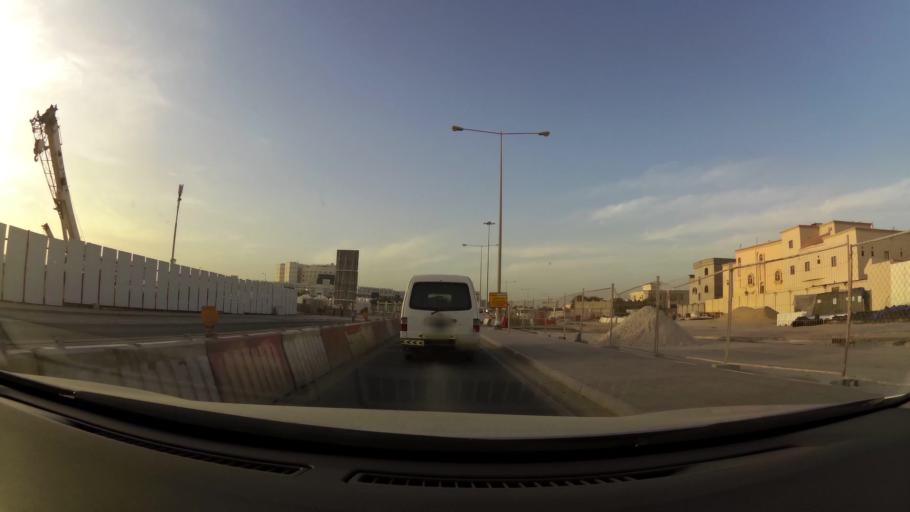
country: QA
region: Al Wakrah
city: Al Wakrah
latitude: 25.1635
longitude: 51.5902
